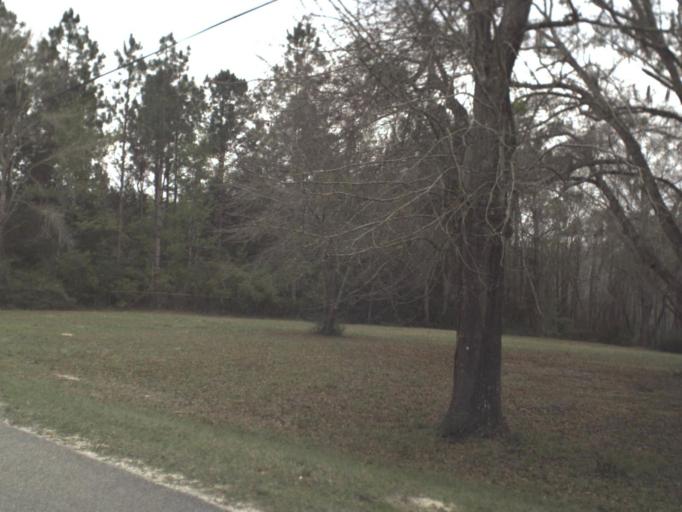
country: US
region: Florida
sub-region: Gulf County
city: Wewahitchka
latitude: 30.1427
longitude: -85.2104
